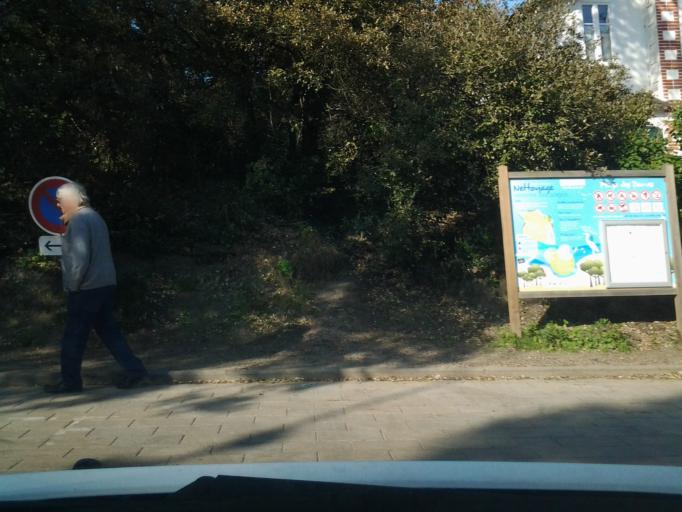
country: FR
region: Pays de la Loire
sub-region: Departement de la Vendee
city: La Gueriniere
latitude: 47.0097
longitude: -2.2215
